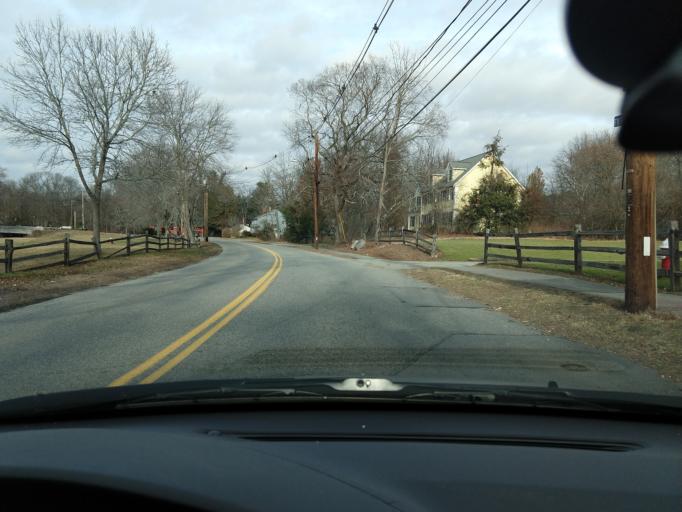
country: US
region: Massachusetts
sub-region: Middlesex County
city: Bedford
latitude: 42.4917
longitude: -71.2558
